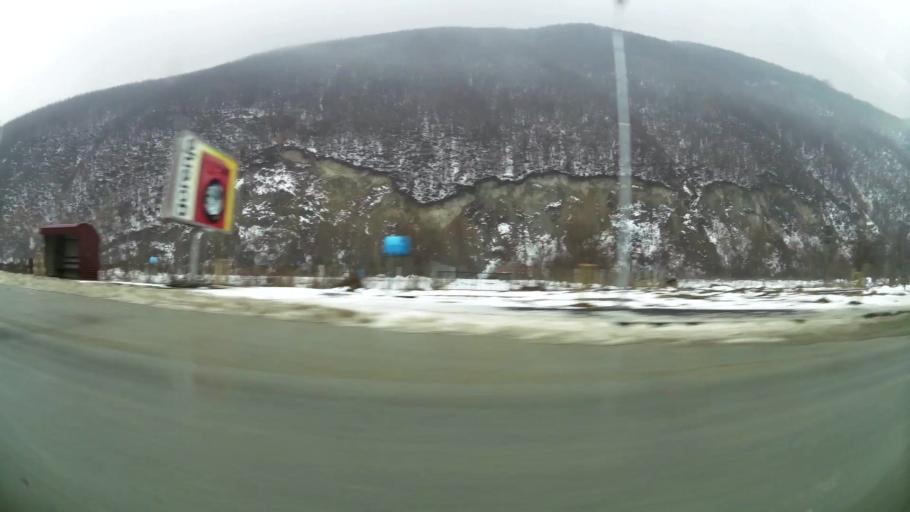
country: XK
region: Ferizaj
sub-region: Hani i Elezit
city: Hani i Elezit
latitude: 42.1614
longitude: 21.2796
